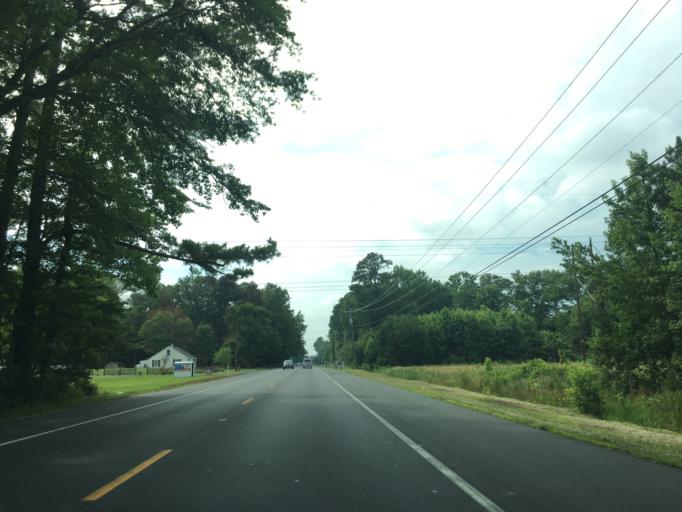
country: US
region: Delaware
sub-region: Sussex County
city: Millsboro
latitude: 38.5612
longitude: -75.2672
